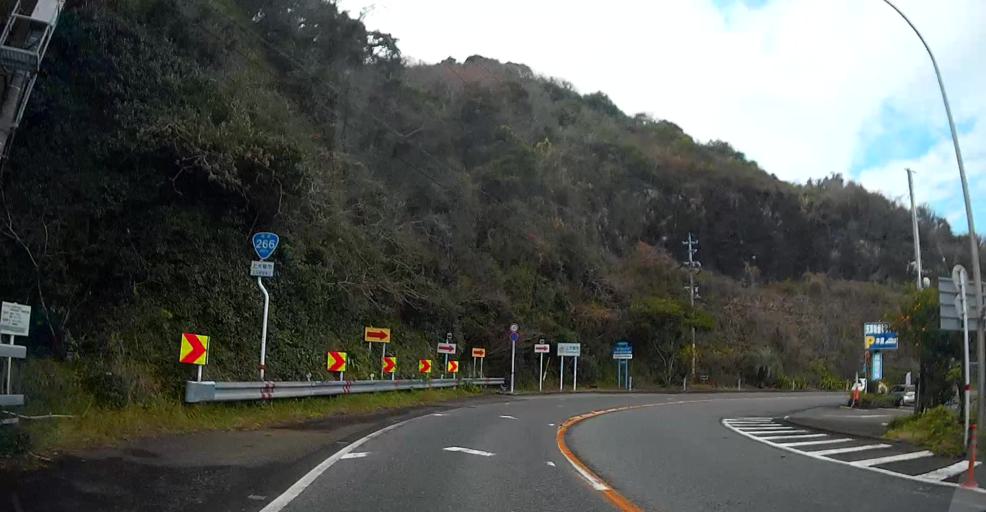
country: JP
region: Kumamoto
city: Yatsushiro
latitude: 32.6118
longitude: 130.4566
